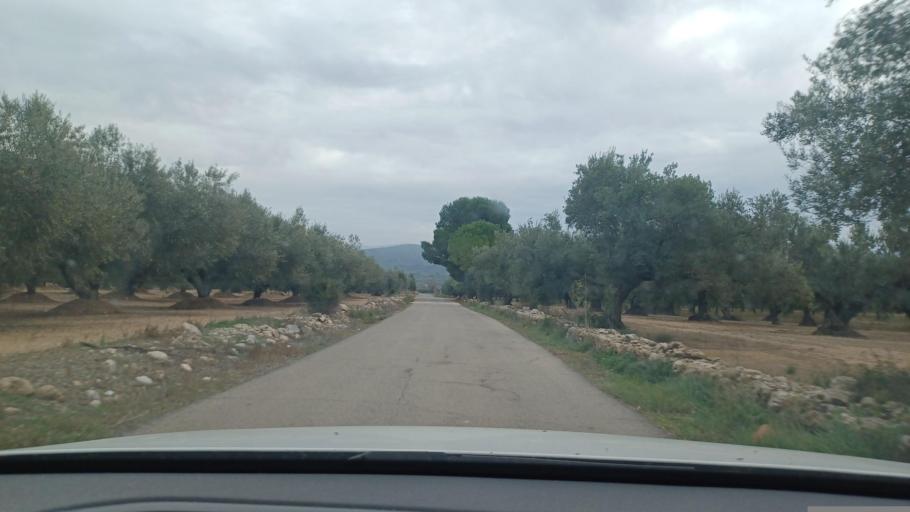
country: ES
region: Catalonia
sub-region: Provincia de Tarragona
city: Santa Barbara
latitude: 40.6669
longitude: 0.4450
